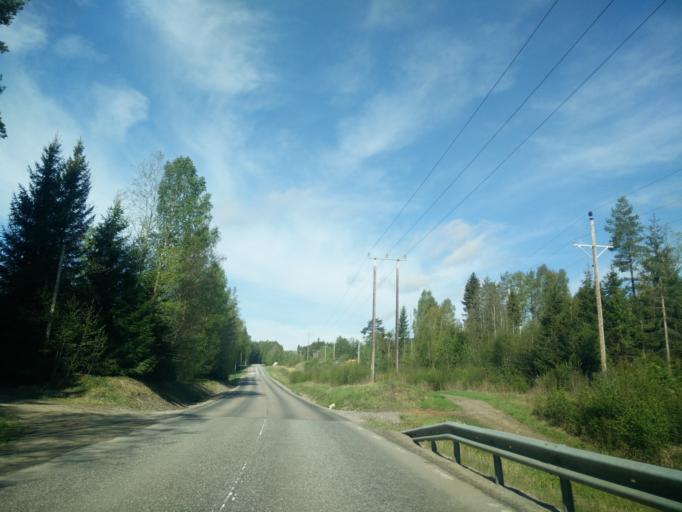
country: SE
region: Vaesternorrland
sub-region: Sundsvalls Kommun
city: Nolby
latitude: 62.2992
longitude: 17.3287
